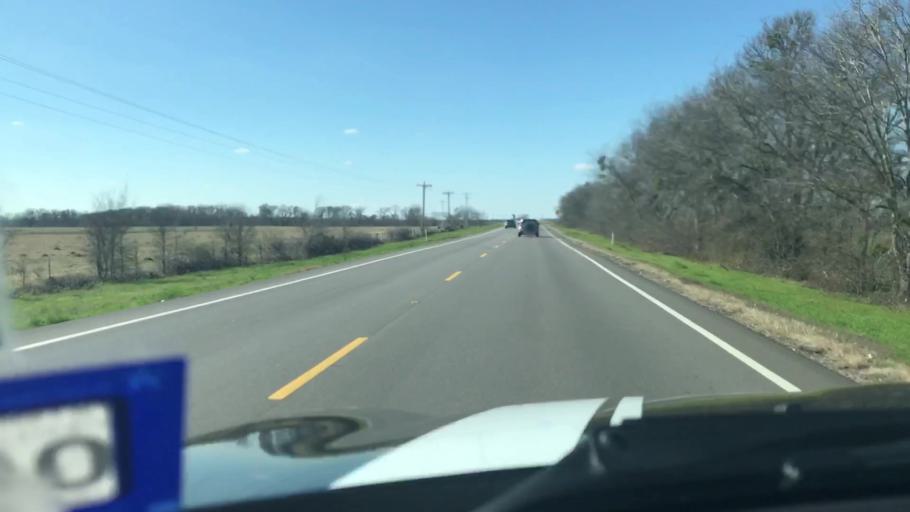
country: US
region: Texas
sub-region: Robertson County
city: Hearne
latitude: 30.8817
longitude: -96.6338
